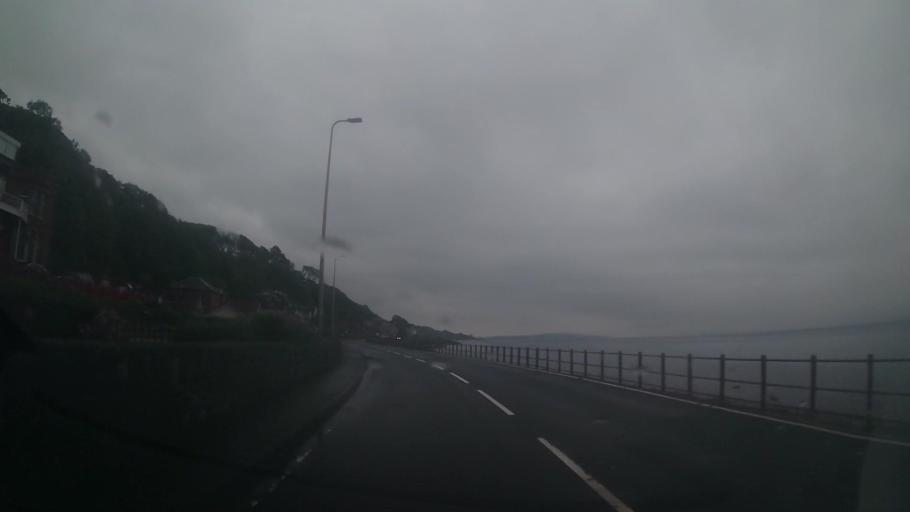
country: GB
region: Scotland
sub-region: North Ayrshire
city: Skelmorlie
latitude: 55.8629
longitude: -4.8903
